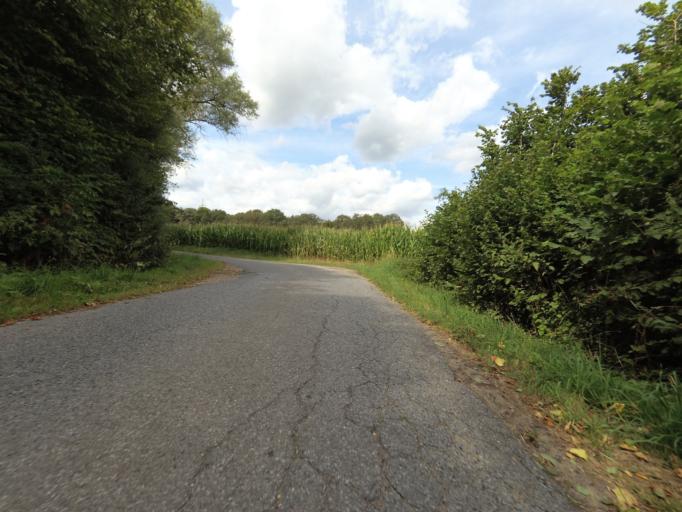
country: DE
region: North Rhine-Westphalia
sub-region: Regierungsbezirk Munster
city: Ahaus
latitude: 52.1459
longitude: 6.9903
